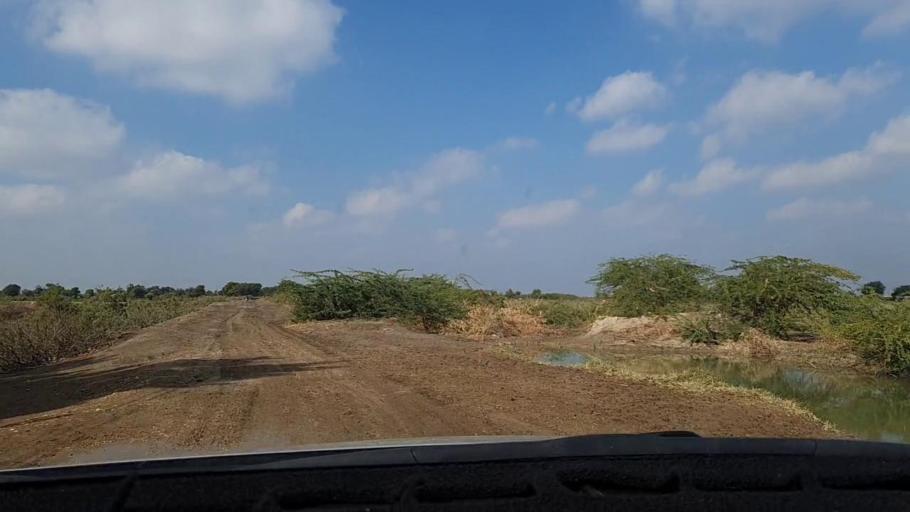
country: PK
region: Sindh
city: Tando Mittha Khan
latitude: 25.7747
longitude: 69.2578
